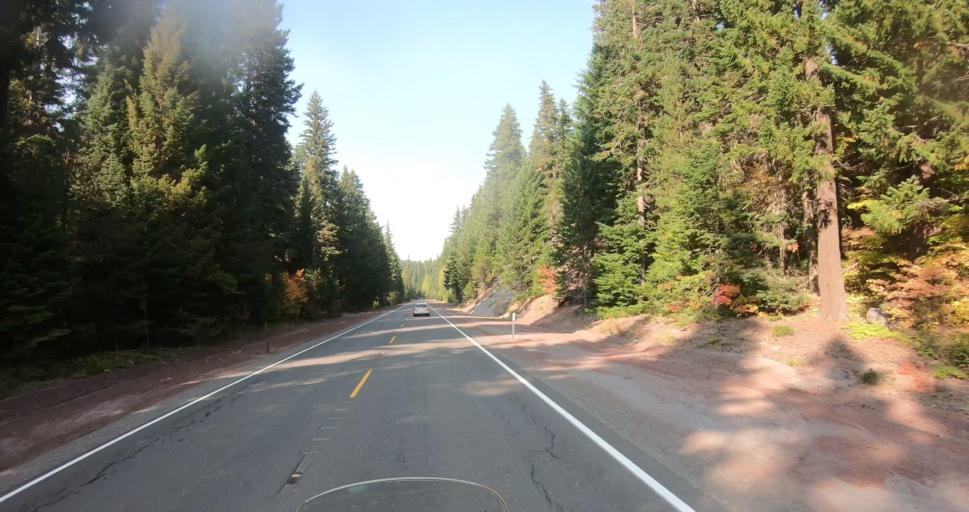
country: US
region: Oregon
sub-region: Hood River County
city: Odell
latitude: 45.3879
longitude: -121.5690
